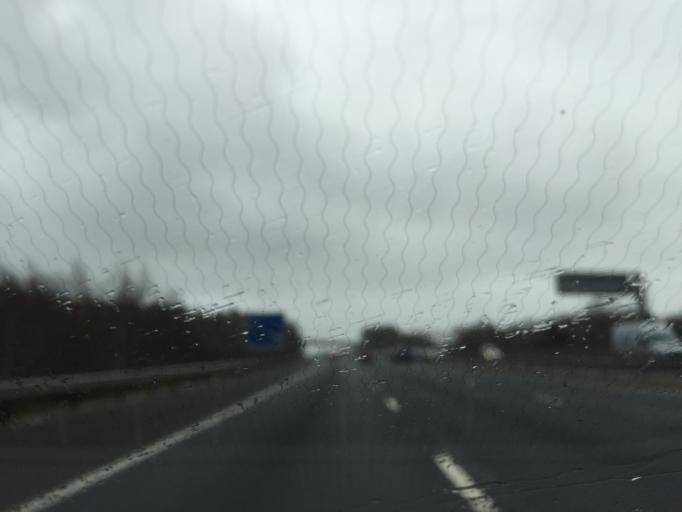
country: GB
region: England
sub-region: Hampshire
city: Botley
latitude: 50.8785
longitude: -1.2732
